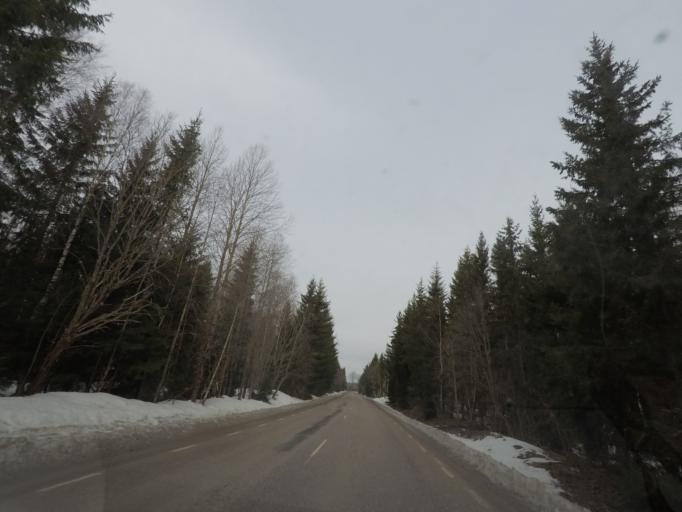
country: SE
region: Vaestmanland
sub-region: Vasteras
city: Skultuna
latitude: 59.7459
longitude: 16.3600
